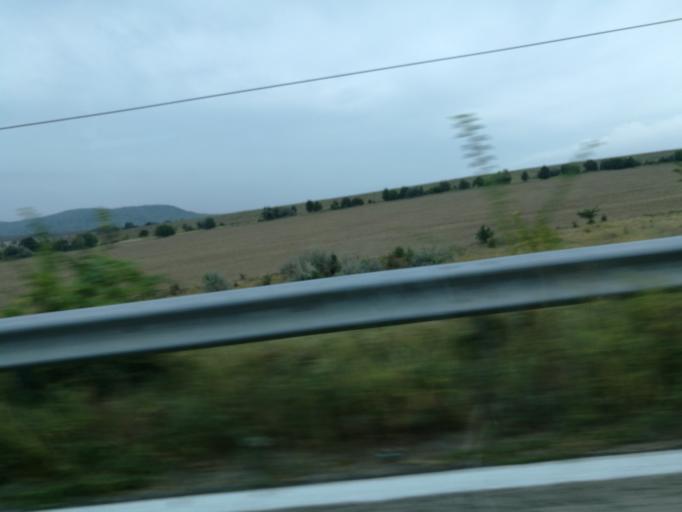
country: RO
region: Tulcea
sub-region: Comuna Horia
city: Horia
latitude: 44.9800
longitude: 28.4444
